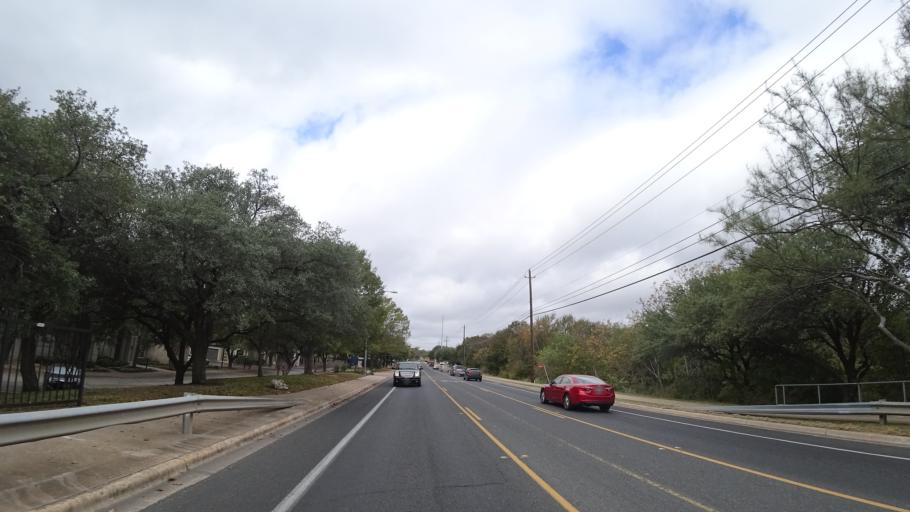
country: US
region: Texas
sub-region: Williamson County
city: Jollyville
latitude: 30.4117
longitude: -97.7267
